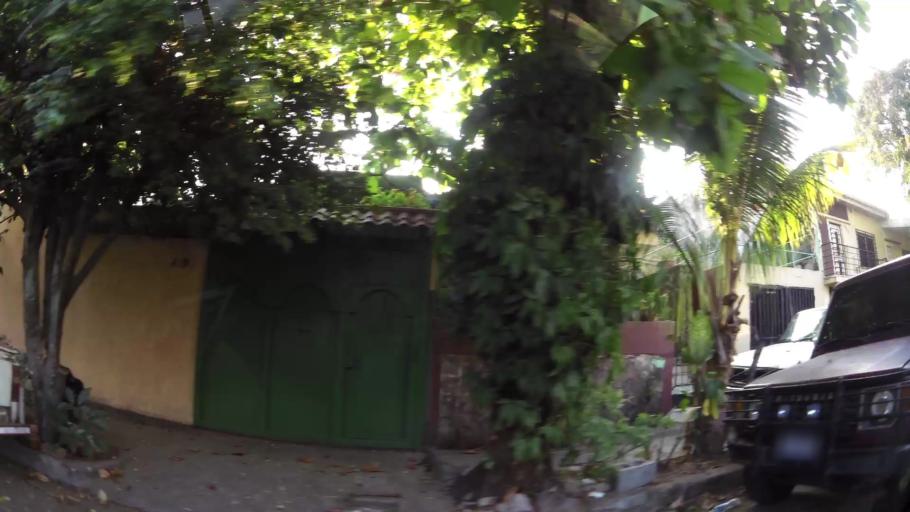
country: SV
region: San Salvador
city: San Salvador
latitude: 13.6793
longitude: -89.2004
